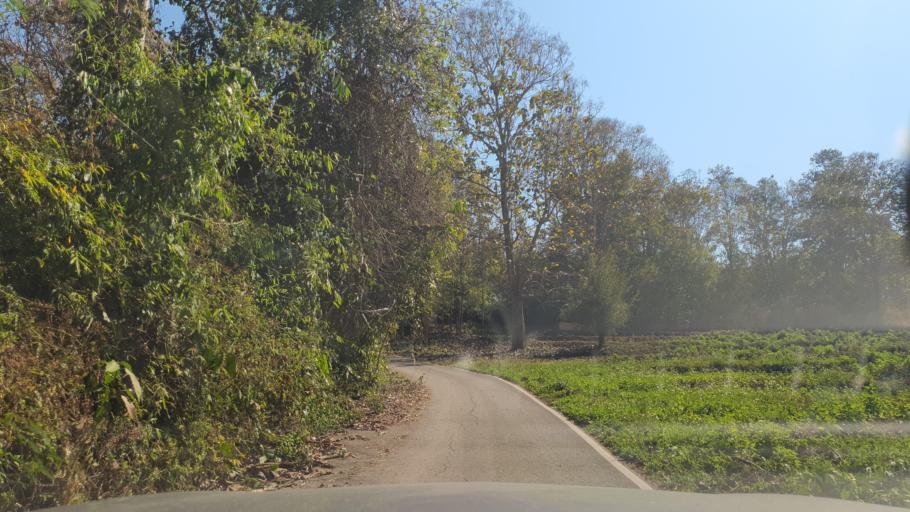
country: TH
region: Chiang Mai
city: Mae On
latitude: 18.8735
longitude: 99.2619
